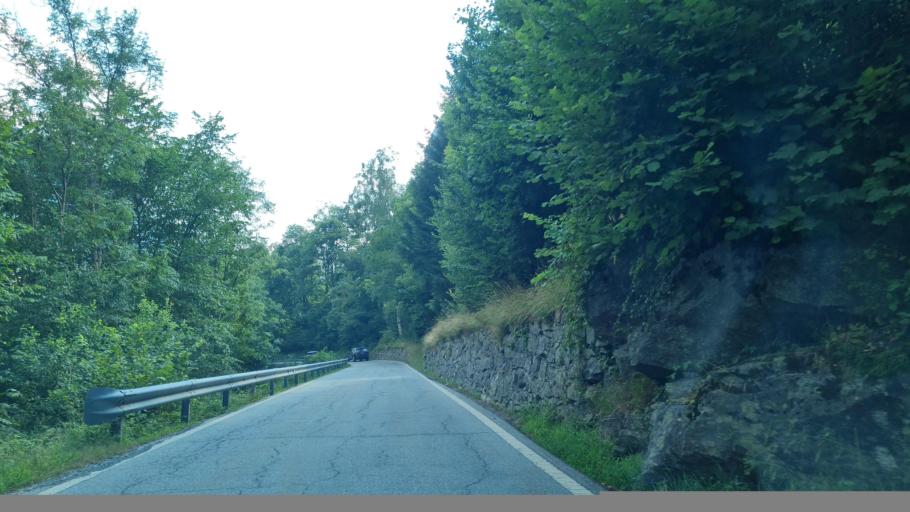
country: IT
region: Piedmont
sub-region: Provincia Verbano-Cusio-Ossola
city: Formazza
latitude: 46.3231
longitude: 8.3870
